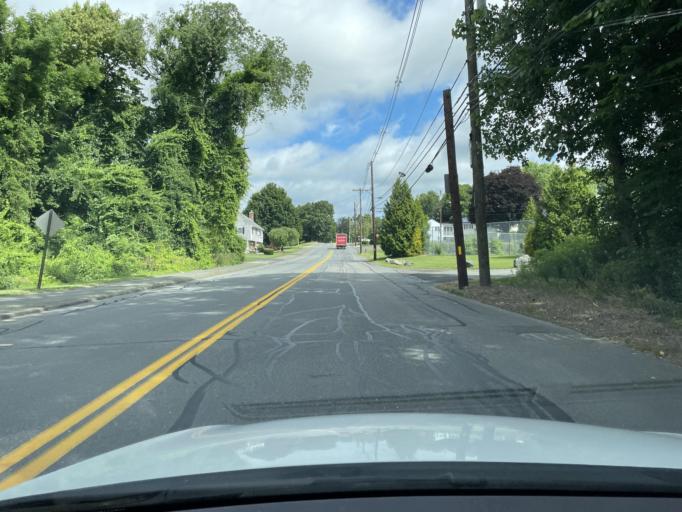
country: US
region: Massachusetts
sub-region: Middlesex County
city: Woburn
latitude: 42.4788
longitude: -71.1736
